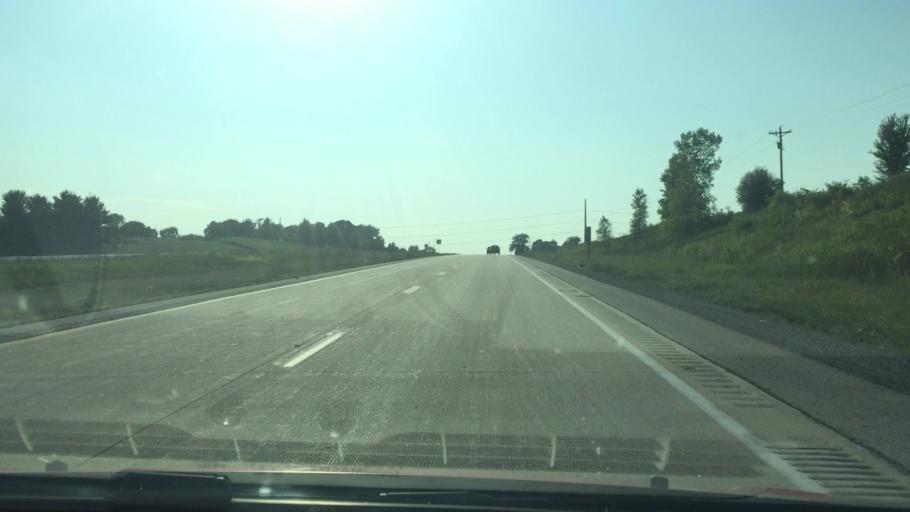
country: US
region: Iowa
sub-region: Scott County
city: Blue Grass
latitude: 41.5135
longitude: -90.8067
